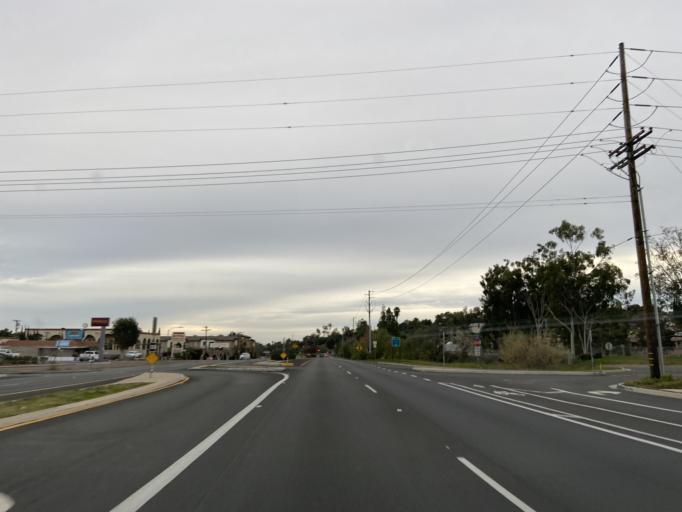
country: US
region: California
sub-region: San Diego County
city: Escondido
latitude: 33.0947
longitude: -117.0719
